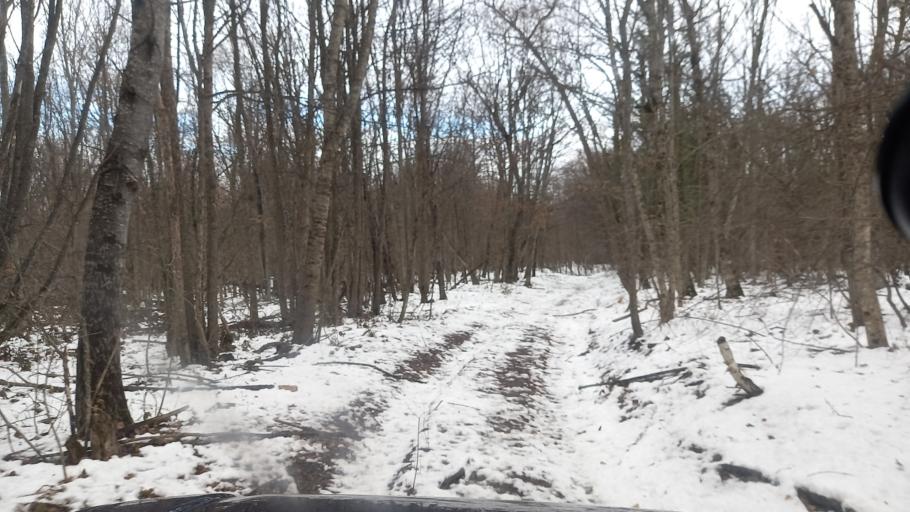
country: RU
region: Adygeya
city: Kamennomostskiy
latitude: 44.2544
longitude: 40.1820
